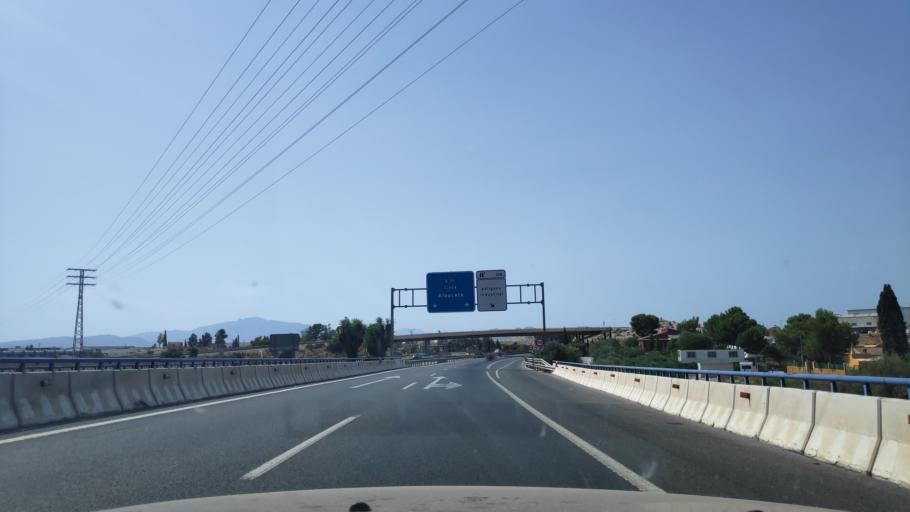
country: ES
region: Murcia
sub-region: Murcia
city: Molina de Segura
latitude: 38.0812
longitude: -1.2178
